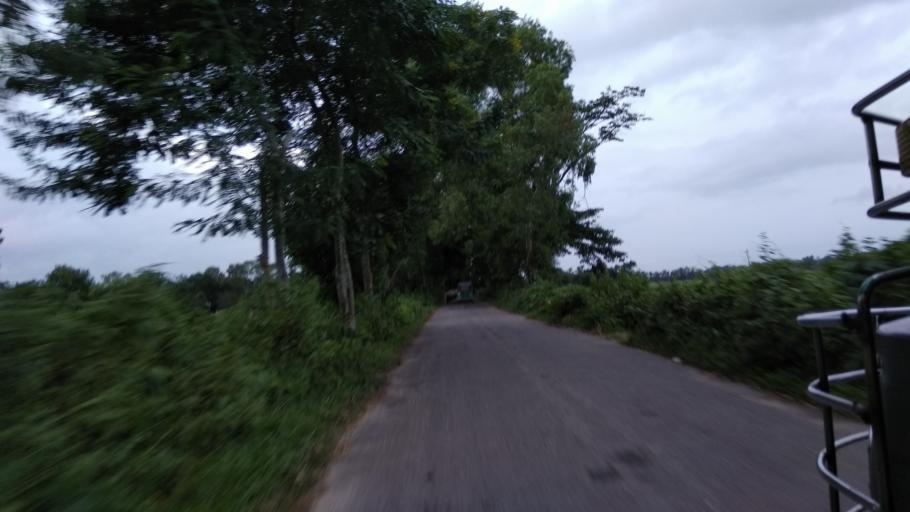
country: IN
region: Tripura
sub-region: Dhalai
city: Kamalpur
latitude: 24.2189
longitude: 91.8546
